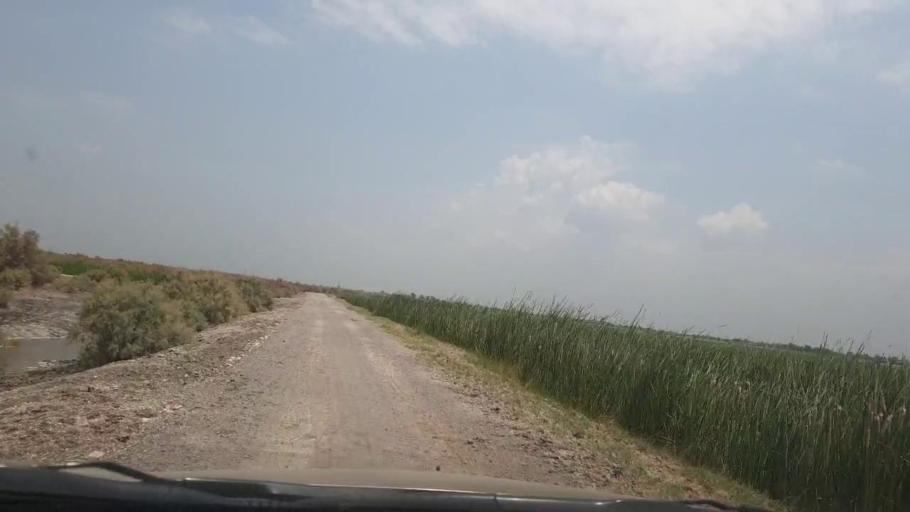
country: PK
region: Sindh
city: Naudero
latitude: 27.7221
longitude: 68.3200
